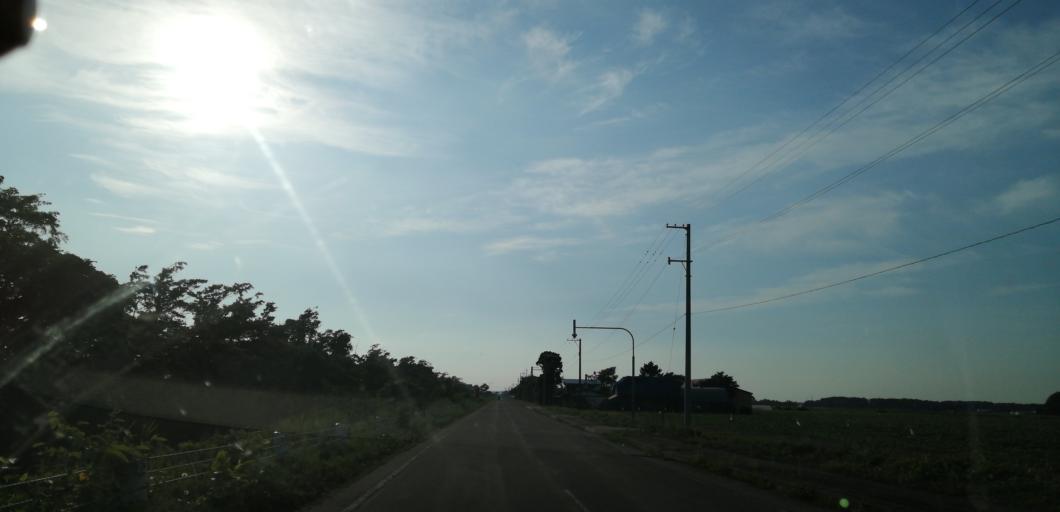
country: JP
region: Hokkaido
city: Kitahiroshima
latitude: 42.9495
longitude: 141.6726
